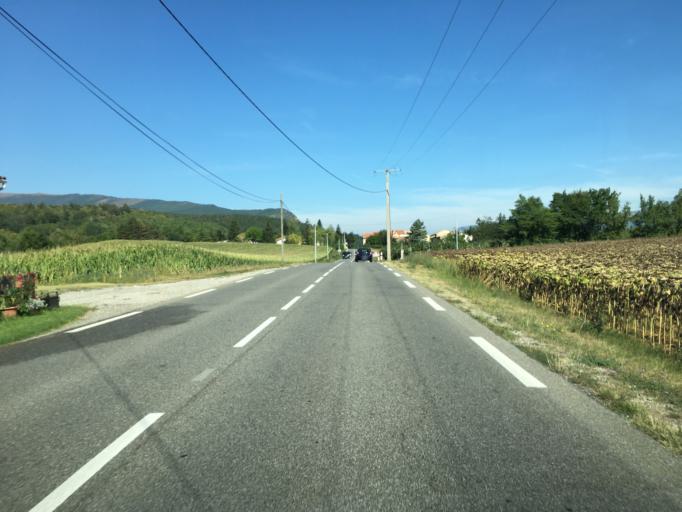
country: FR
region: Provence-Alpes-Cote d'Azur
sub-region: Departement des Hautes-Alpes
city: Laragne-Monteglin
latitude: 44.2778
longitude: 5.8509
